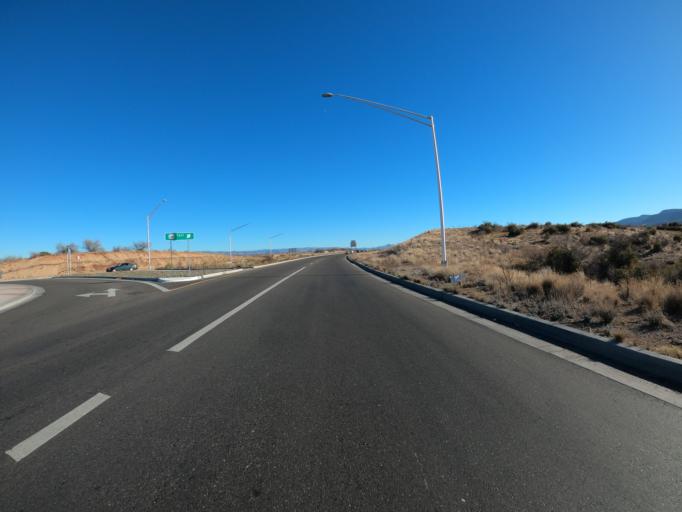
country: US
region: Arizona
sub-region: Yavapai County
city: Cornville
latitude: 34.6283
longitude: -111.9338
